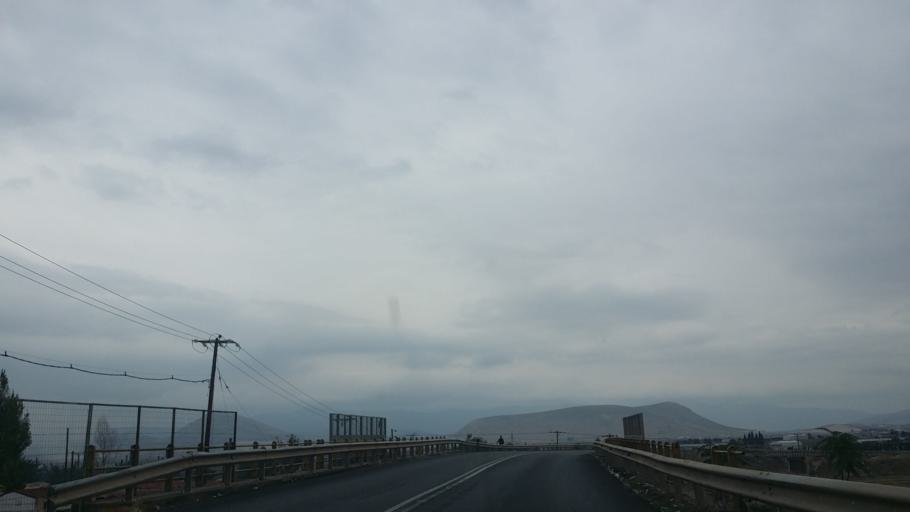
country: GR
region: Central Greece
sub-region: Nomos Voiotias
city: Thivai
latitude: 38.3292
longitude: 23.3033
